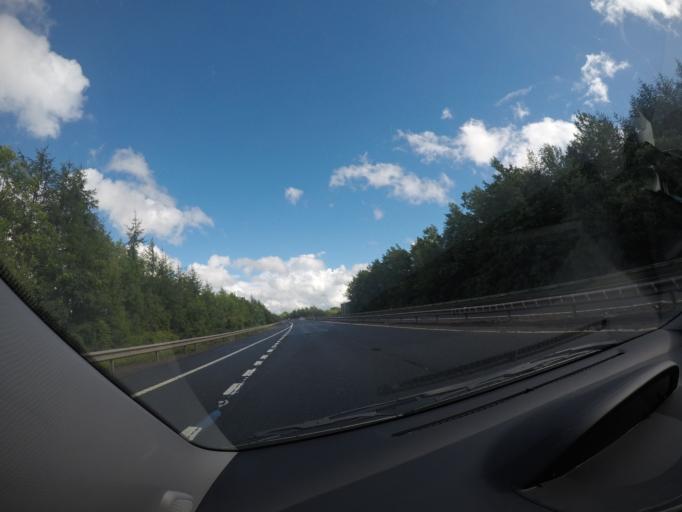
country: GB
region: Scotland
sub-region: South Lanarkshire
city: Lesmahagow
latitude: 55.6470
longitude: -3.8865
